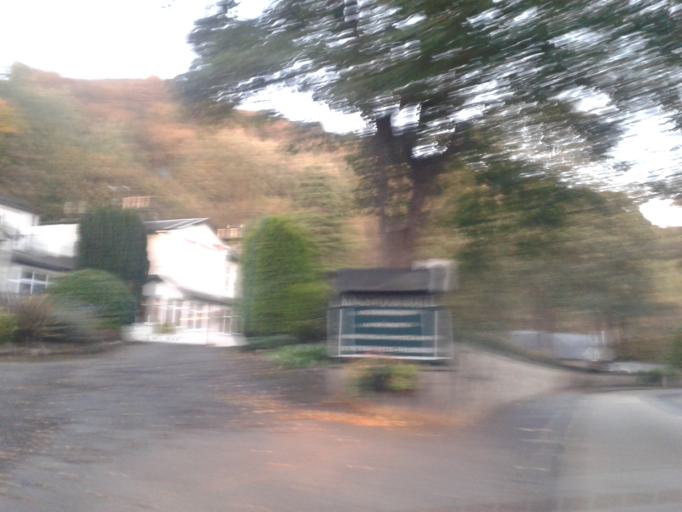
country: GB
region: Scotland
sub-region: Fife
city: Burntisland
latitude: 56.0649
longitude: -3.2050
